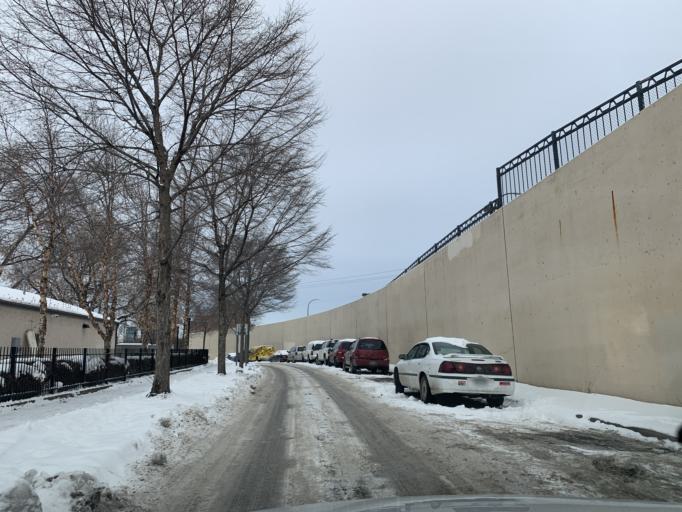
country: US
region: Minnesota
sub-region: Hennepin County
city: Minneapolis
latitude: 44.9586
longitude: -93.2459
